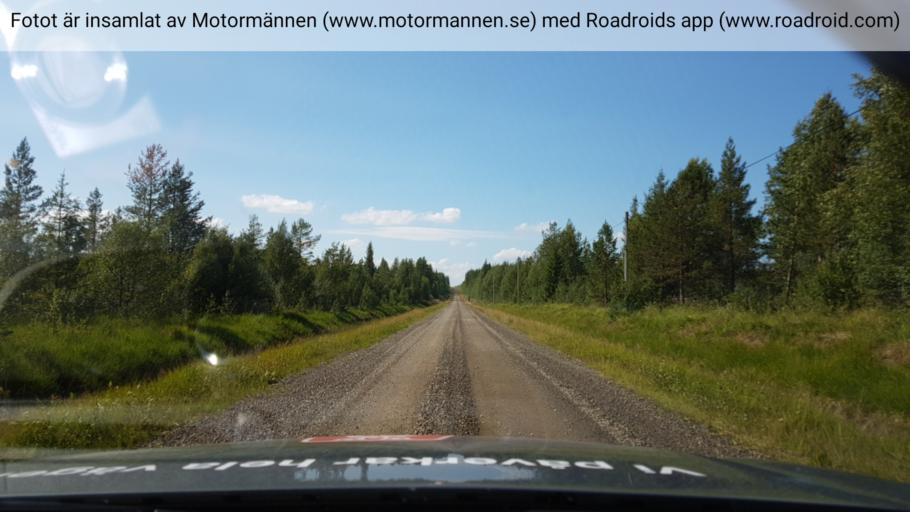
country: SE
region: Vaesterbotten
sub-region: Dorotea Kommun
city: Dorotea
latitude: 64.0905
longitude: 16.5215
